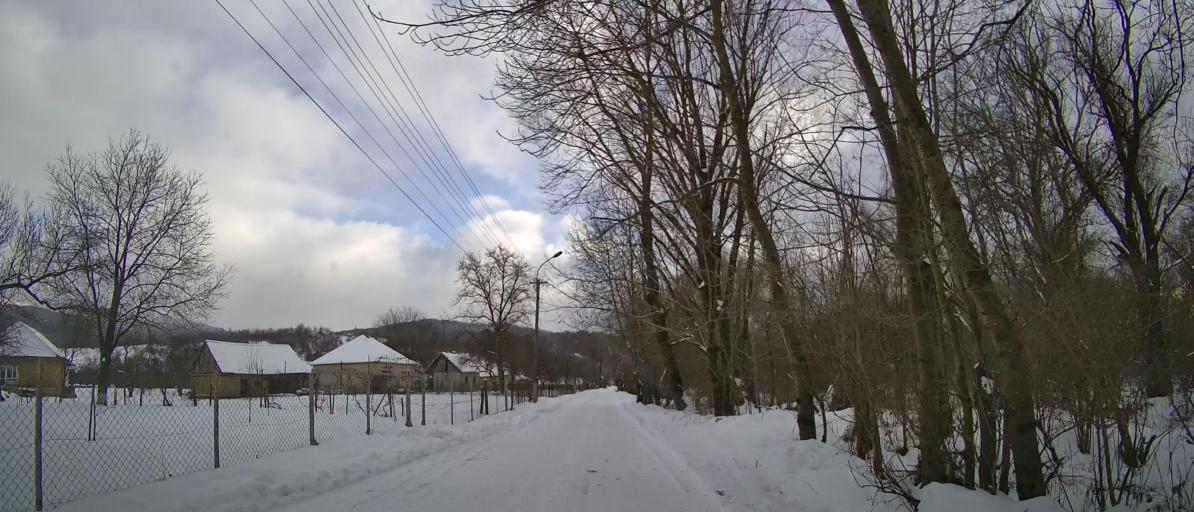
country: UA
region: Zakarpattia
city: Velykyi Bereznyi
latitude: 48.9116
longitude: 22.4650
